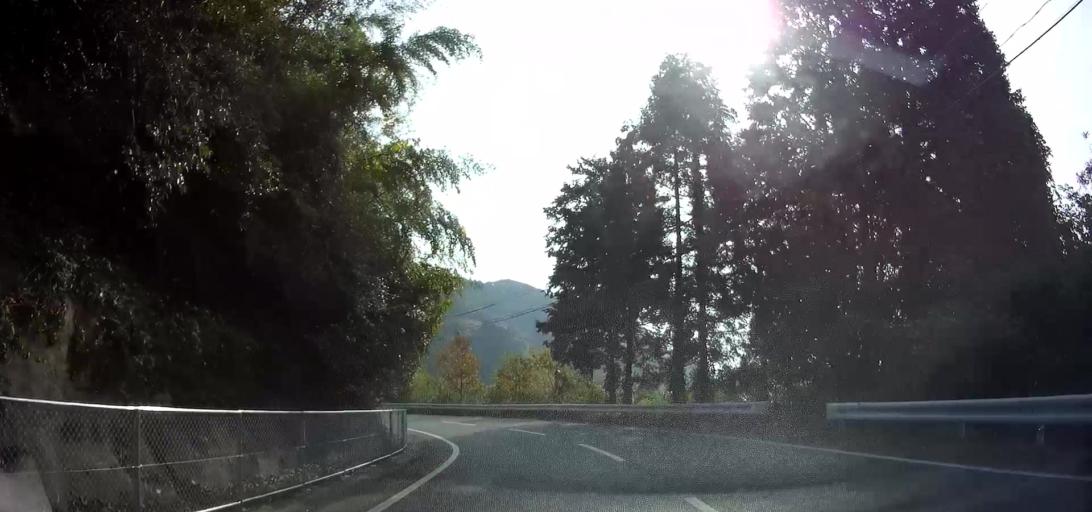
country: JP
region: Nagasaki
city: Shimabara
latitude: 32.6766
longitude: 130.2126
